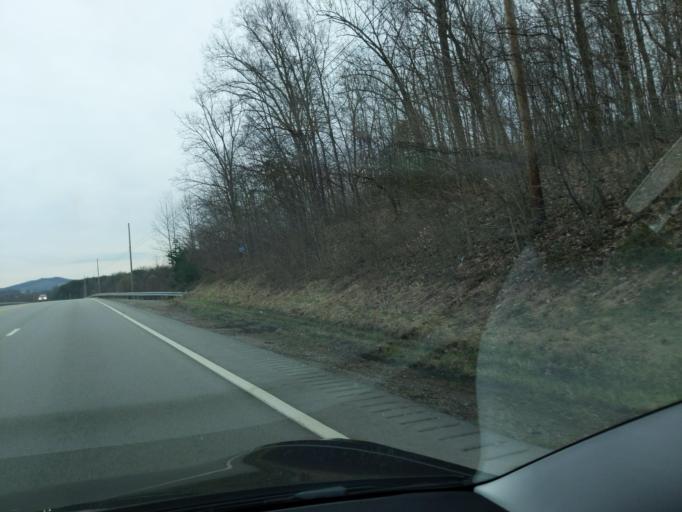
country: US
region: Kentucky
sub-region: Whitley County
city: Corbin
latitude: 36.9183
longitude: -84.1038
